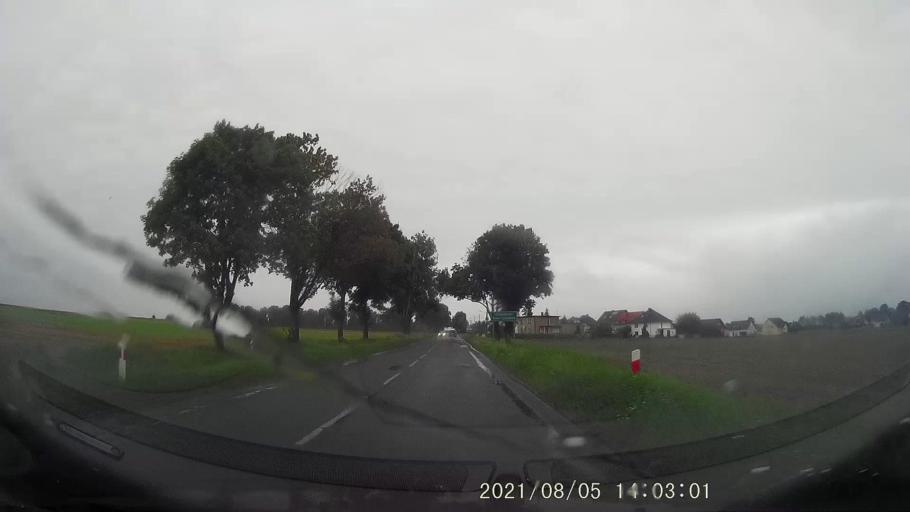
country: PL
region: Opole Voivodeship
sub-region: Powiat krapkowicki
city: Strzeleczki
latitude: 50.4572
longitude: 17.8636
